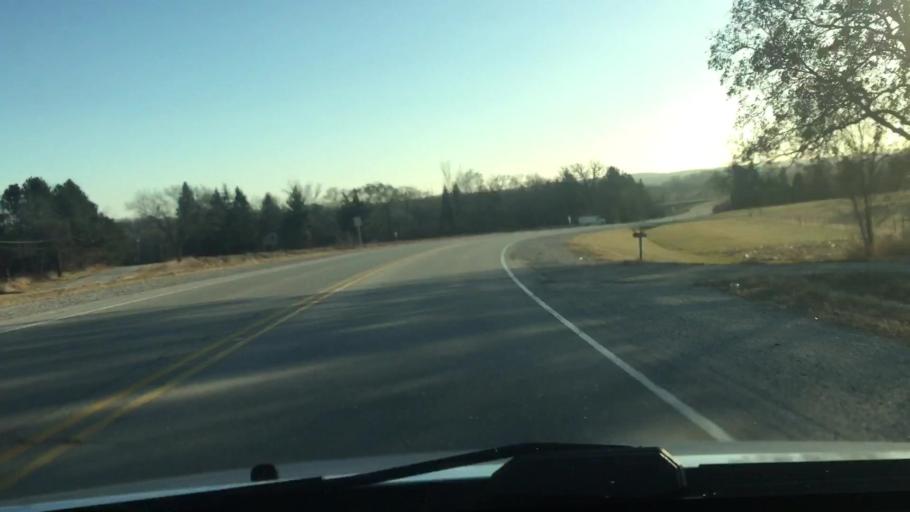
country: US
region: Wisconsin
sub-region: Waukesha County
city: Pewaukee
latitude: 43.0994
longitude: -88.2690
